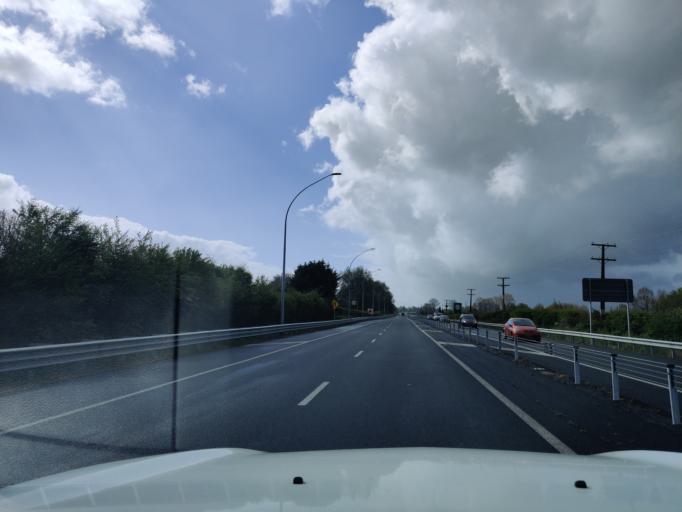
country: NZ
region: Waikato
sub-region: Waipa District
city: Cambridge
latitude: -37.8985
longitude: 175.5110
